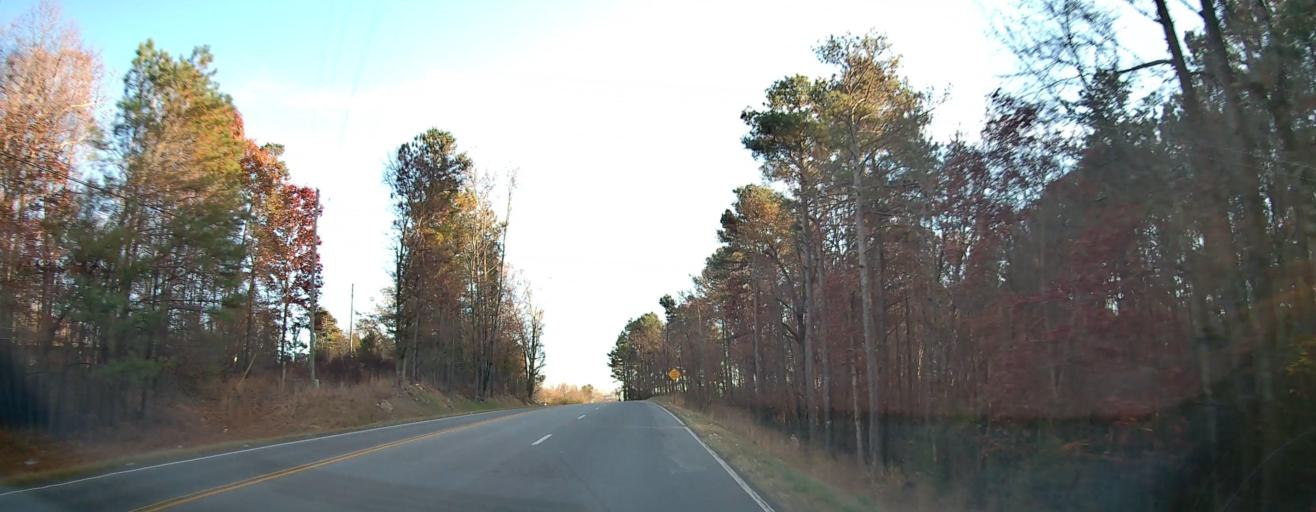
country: US
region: Alabama
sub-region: Blount County
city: Blountsville
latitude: 34.1468
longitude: -86.4513
